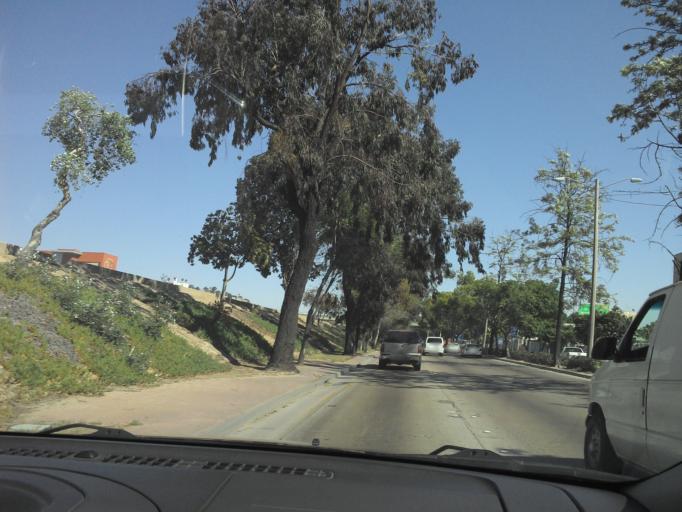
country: MX
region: Baja California
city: Tijuana
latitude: 32.5259
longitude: -117.0141
